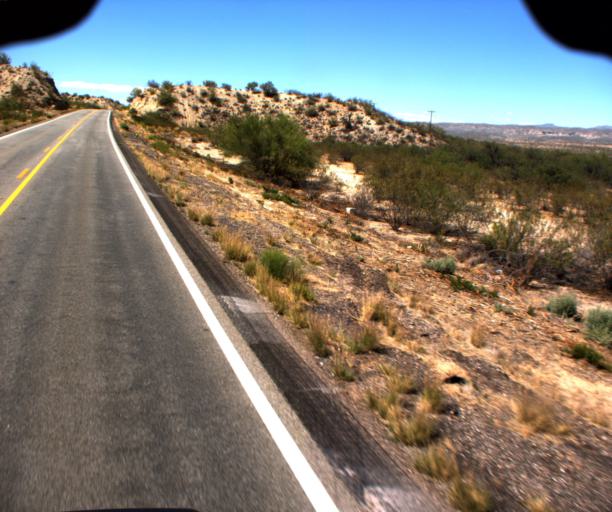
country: US
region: Arizona
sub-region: Yavapai County
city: Bagdad
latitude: 34.7751
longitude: -113.6218
